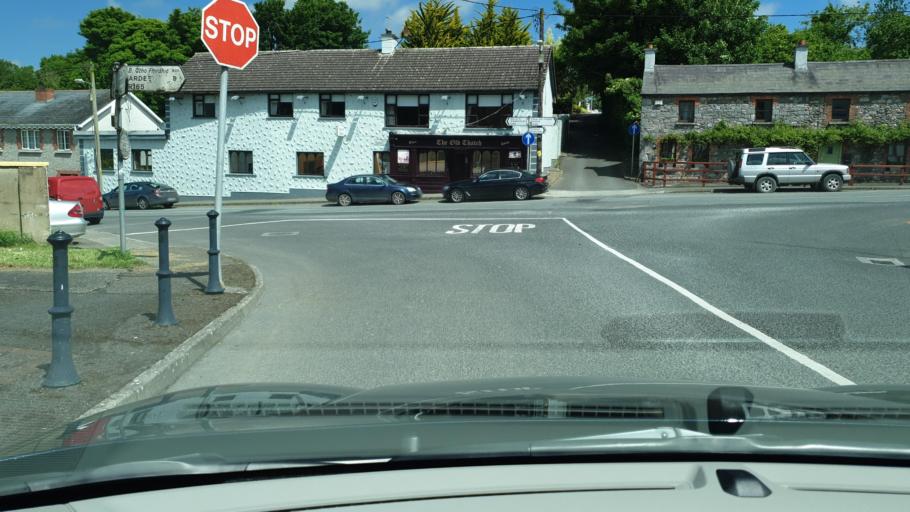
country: IE
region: Leinster
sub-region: Lu
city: Ardee
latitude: 53.8499
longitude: -6.6535
